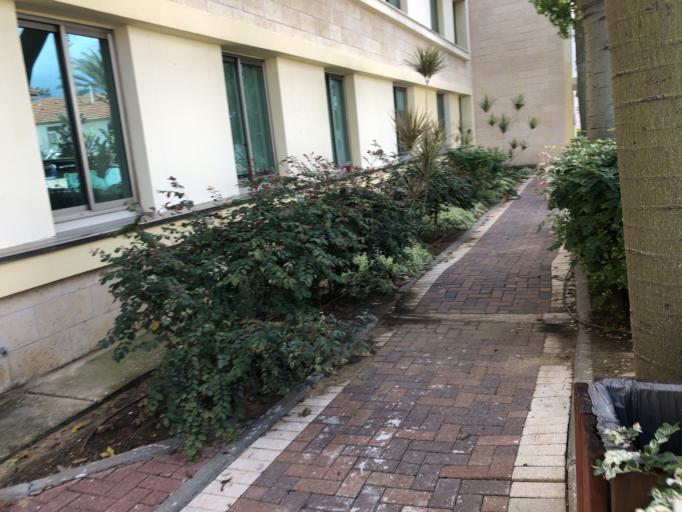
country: IL
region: Central District
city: Ness Ziona
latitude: 31.9304
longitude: 34.8008
